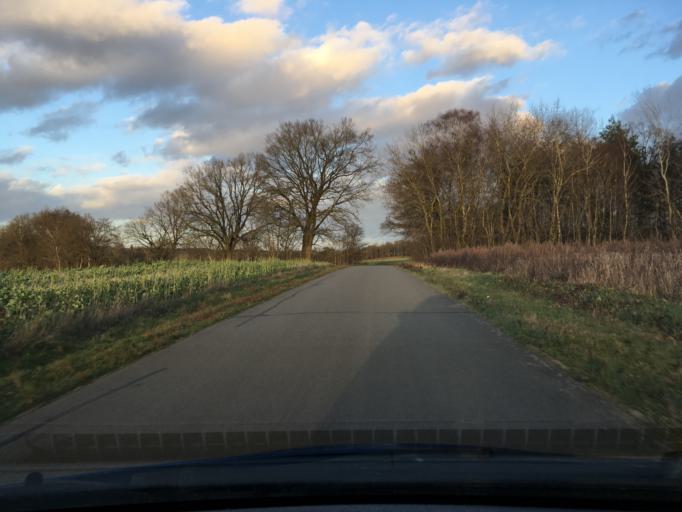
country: DE
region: Lower Saxony
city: Soderstorf
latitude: 53.1322
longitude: 10.1786
